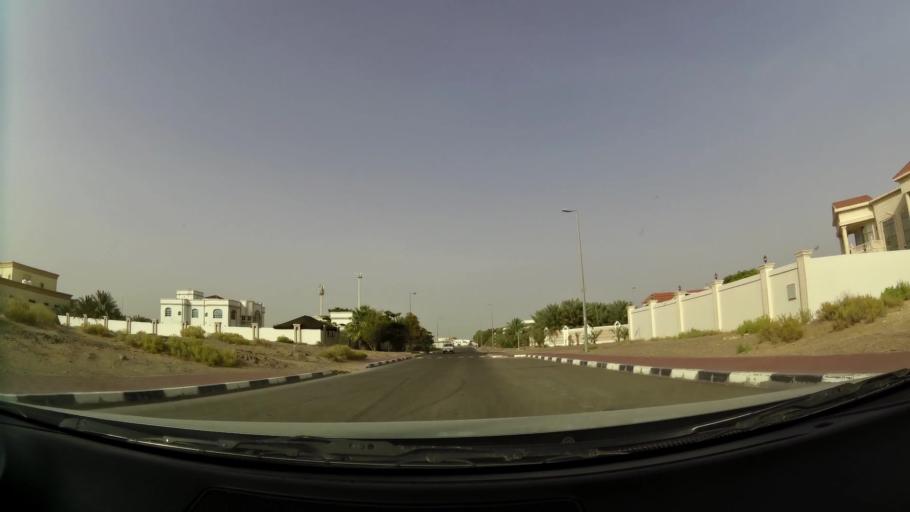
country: AE
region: Abu Dhabi
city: Al Ain
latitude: 24.2192
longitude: 55.6456
